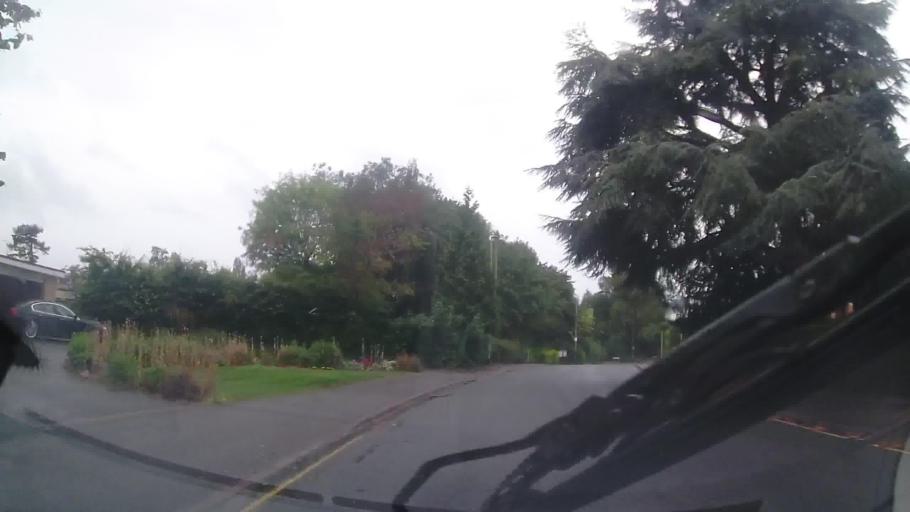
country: GB
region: England
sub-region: Leicestershire
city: Glenfield
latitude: 52.6502
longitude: -1.1854
